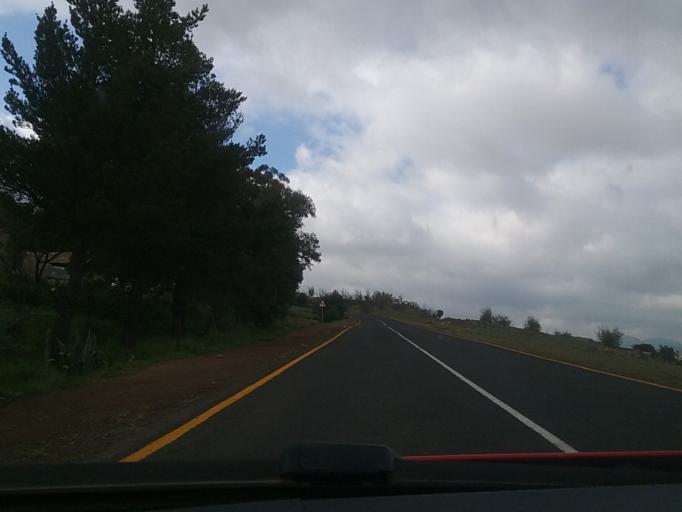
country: LS
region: Berea
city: Teyateyaneng
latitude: -29.1835
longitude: 27.7880
